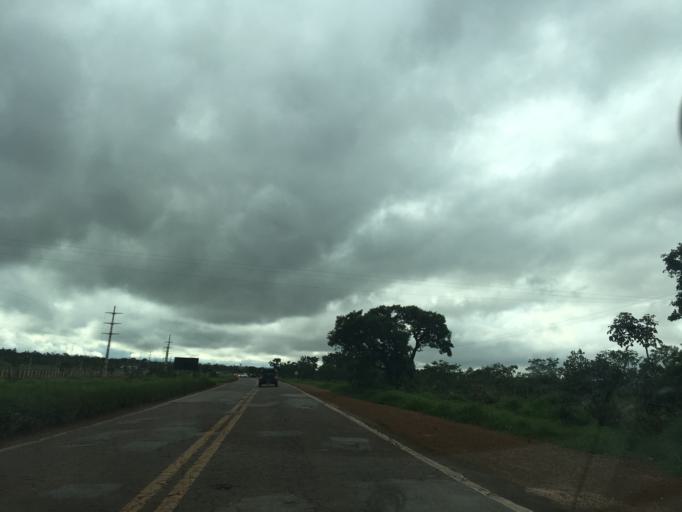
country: BR
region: Federal District
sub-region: Brasilia
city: Brasilia
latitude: -15.9745
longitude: -47.9726
